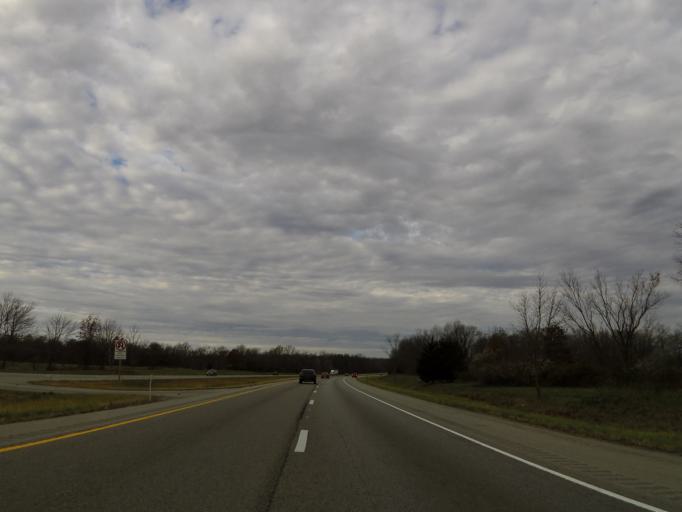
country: US
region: Illinois
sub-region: Clinton County
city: Wamac
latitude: 38.3629
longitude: -89.0799
